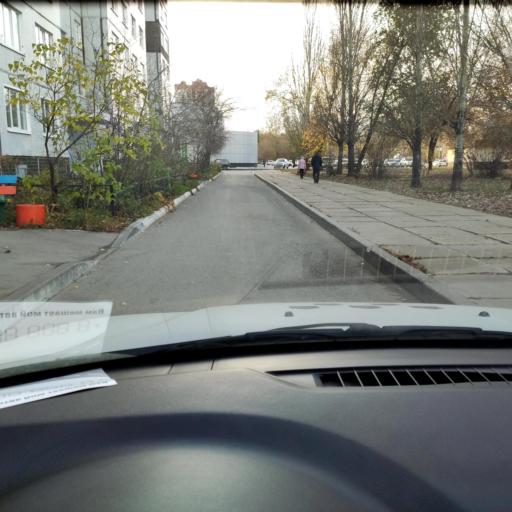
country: RU
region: Samara
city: Tol'yatti
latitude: 53.5101
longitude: 49.4376
